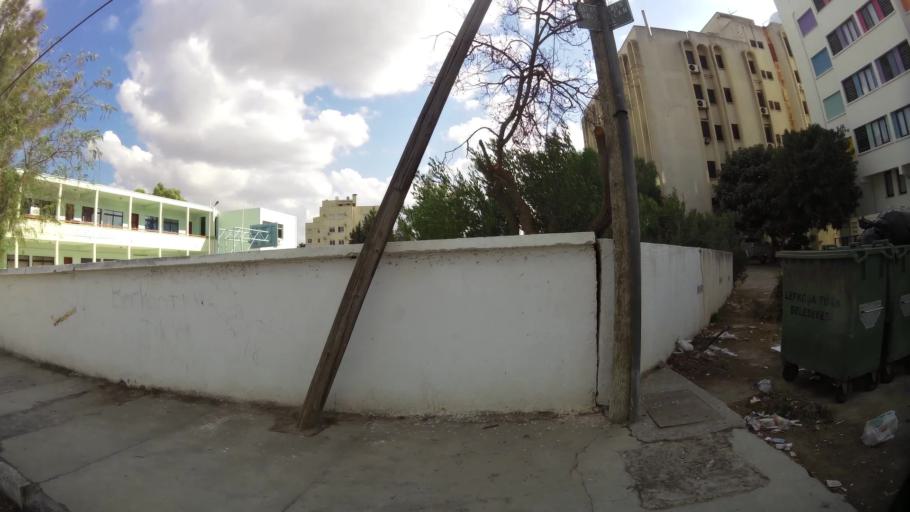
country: CY
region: Lefkosia
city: Nicosia
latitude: 35.1958
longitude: 33.3477
